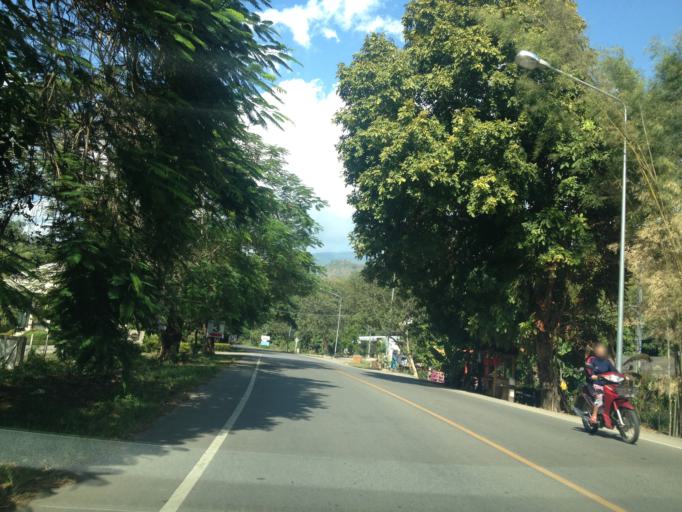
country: TH
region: Chiang Mai
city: Hang Dong
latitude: 18.7480
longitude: 98.8904
